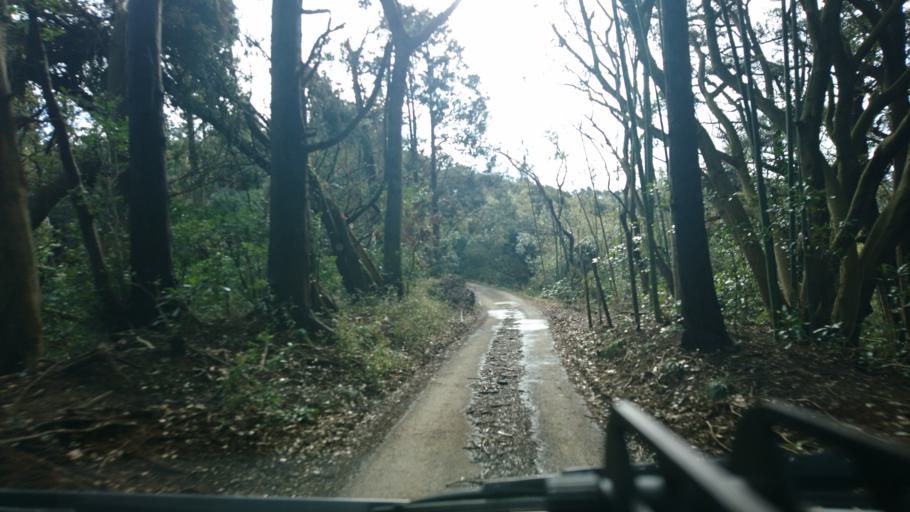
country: JP
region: Chiba
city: Kisarazu
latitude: 35.3316
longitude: 139.9621
